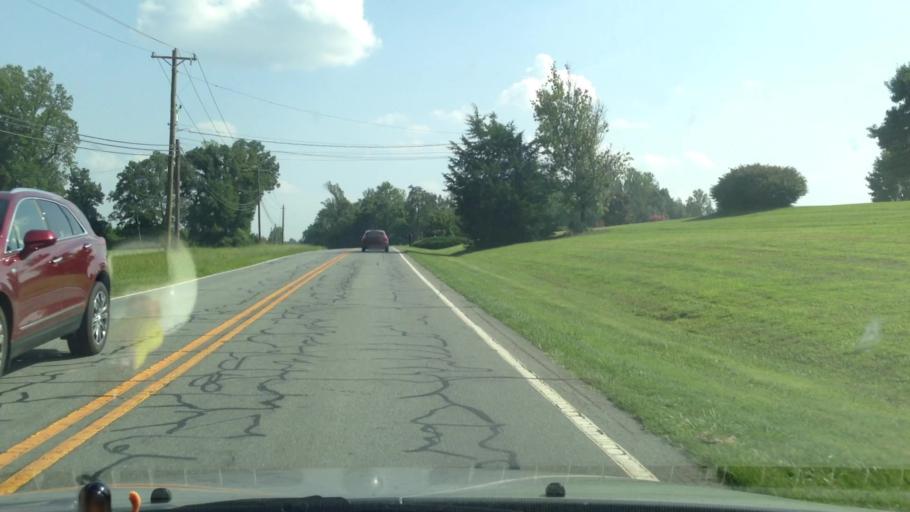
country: US
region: North Carolina
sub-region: Forsyth County
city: Kernersville
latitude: 36.1818
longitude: -80.0614
